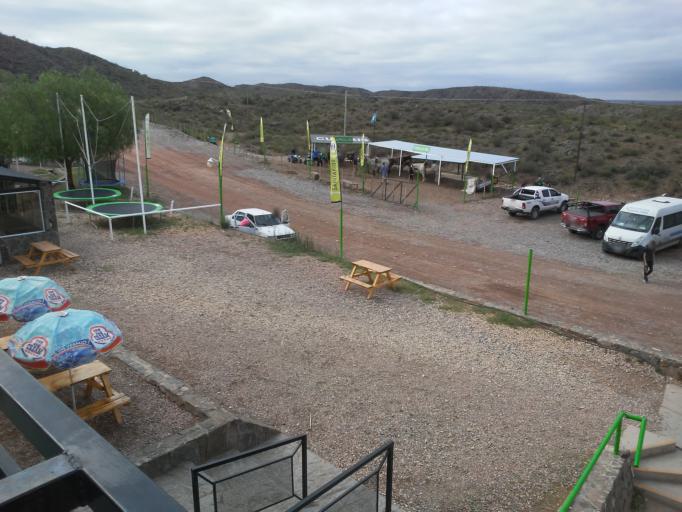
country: AR
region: Mendoza
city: San Rafael
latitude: -34.5939
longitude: -68.6473
